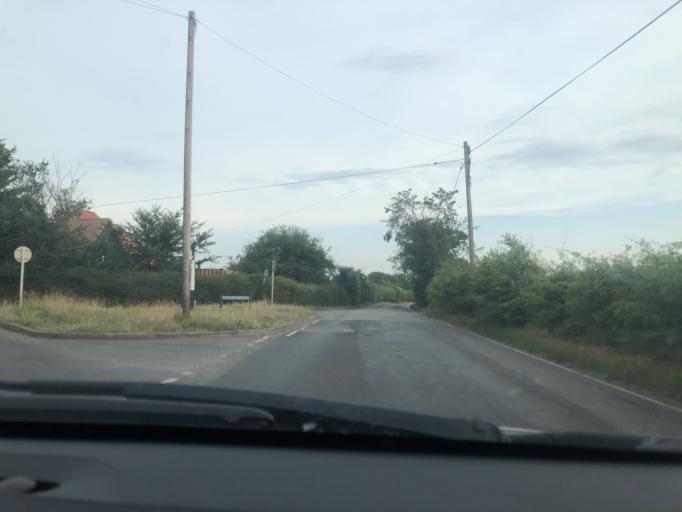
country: GB
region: England
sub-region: Kent
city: Herne Bay
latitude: 51.3441
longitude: 1.1630
